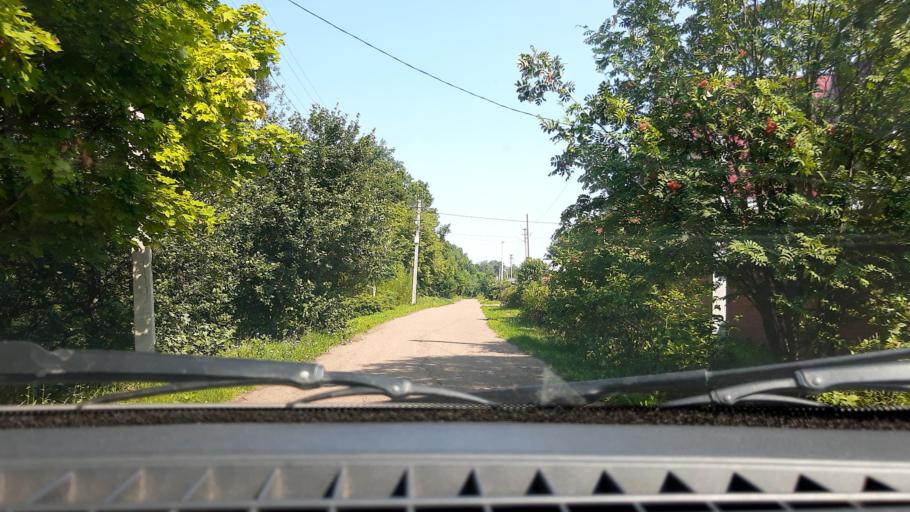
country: RU
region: Bashkortostan
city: Mikhaylovka
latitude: 54.8416
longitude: 55.8272
